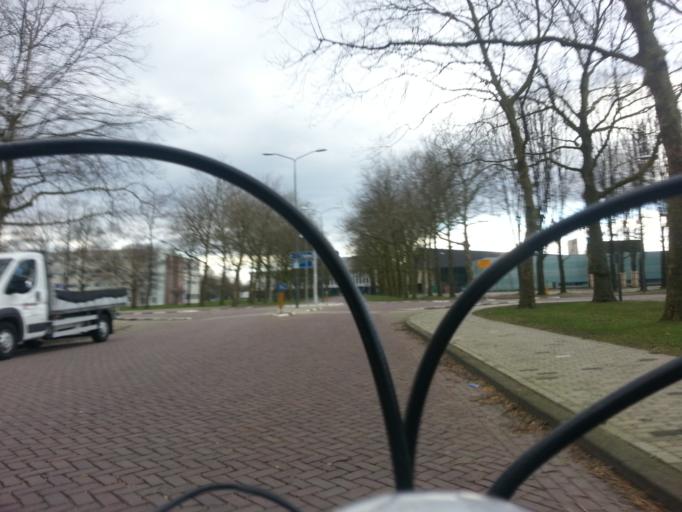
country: NL
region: North Brabant
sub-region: Gemeente Eindhoven
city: Villapark
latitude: 51.4484
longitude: 5.4901
